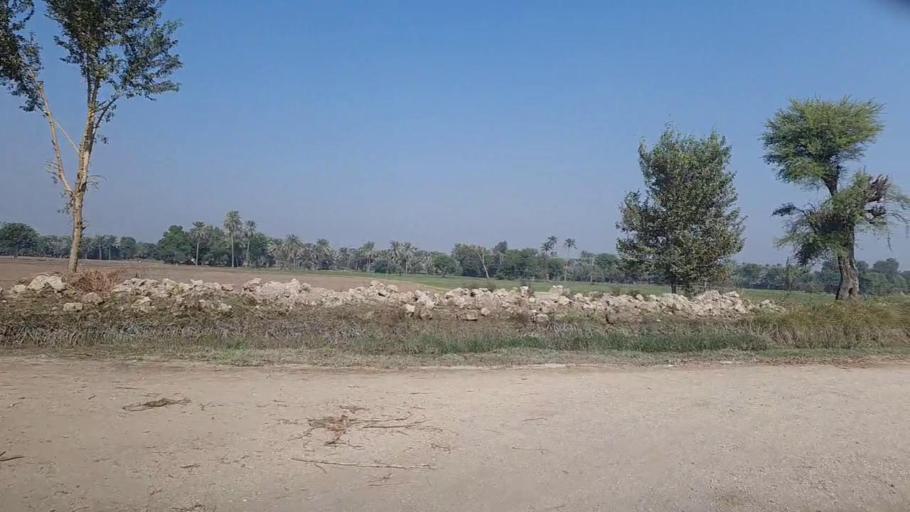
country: PK
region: Sindh
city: Bozdar
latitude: 27.1898
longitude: 68.6112
